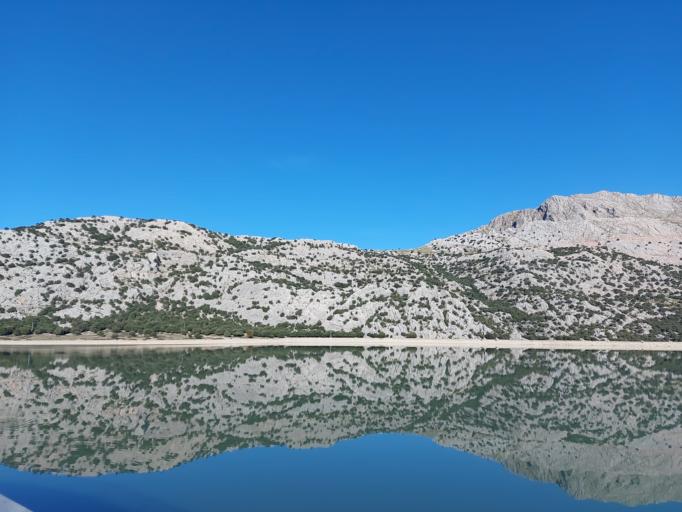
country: ES
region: Balearic Islands
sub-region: Illes Balears
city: Fornalutx
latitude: 39.7807
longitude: 2.7905
